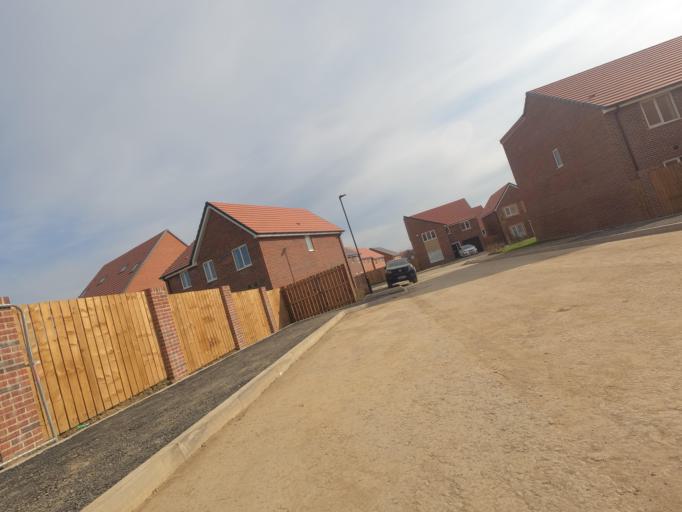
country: GB
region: England
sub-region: Newcastle upon Tyne
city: Dinnington
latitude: 55.0341
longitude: -1.6636
